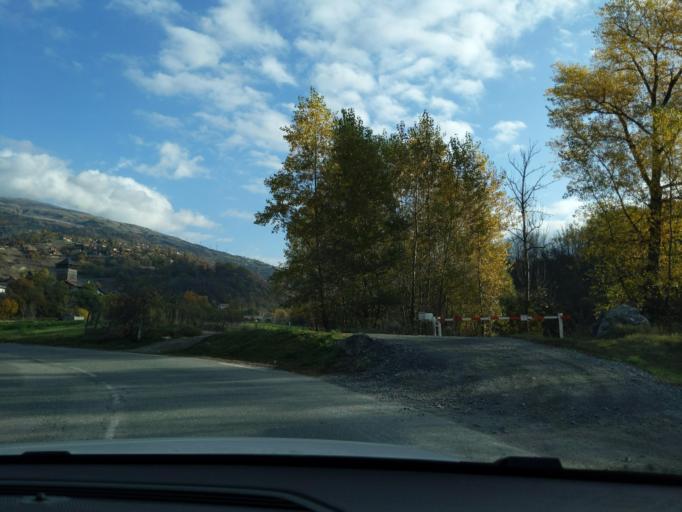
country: FR
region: Rhone-Alpes
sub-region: Departement de la Savoie
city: Aime
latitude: 45.5513
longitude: 6.6491
